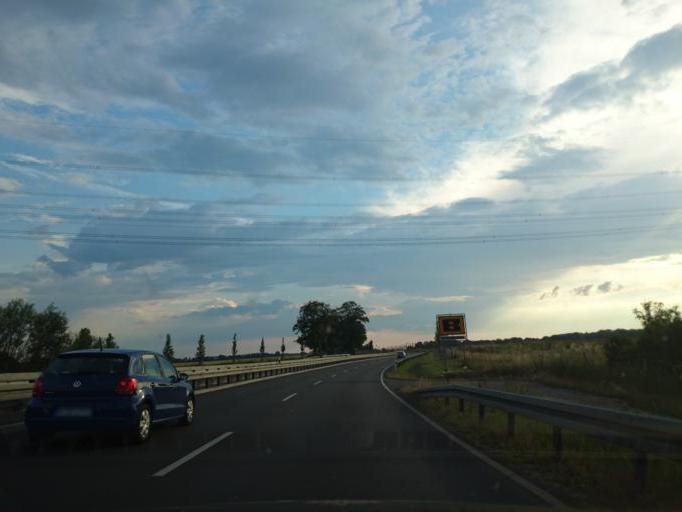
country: DE
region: Brandenburg
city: Neuenhagen
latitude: 52.5501
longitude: 13.6737
